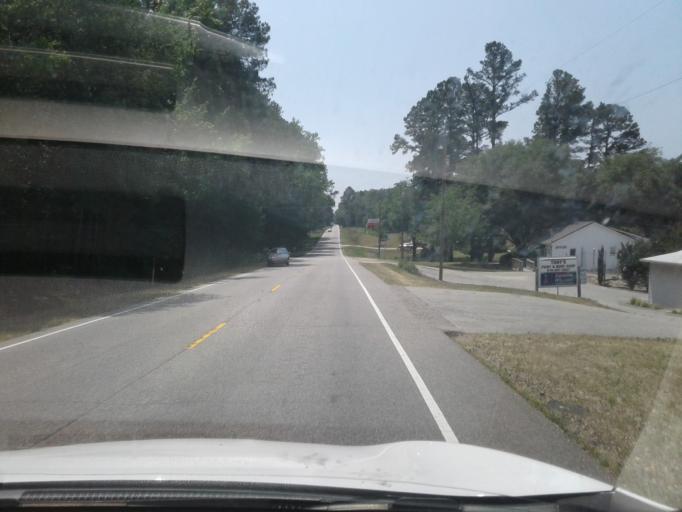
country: US
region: North Carolina
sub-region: Harnett County
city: Coats
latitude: 35.4339
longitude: -78.6796
